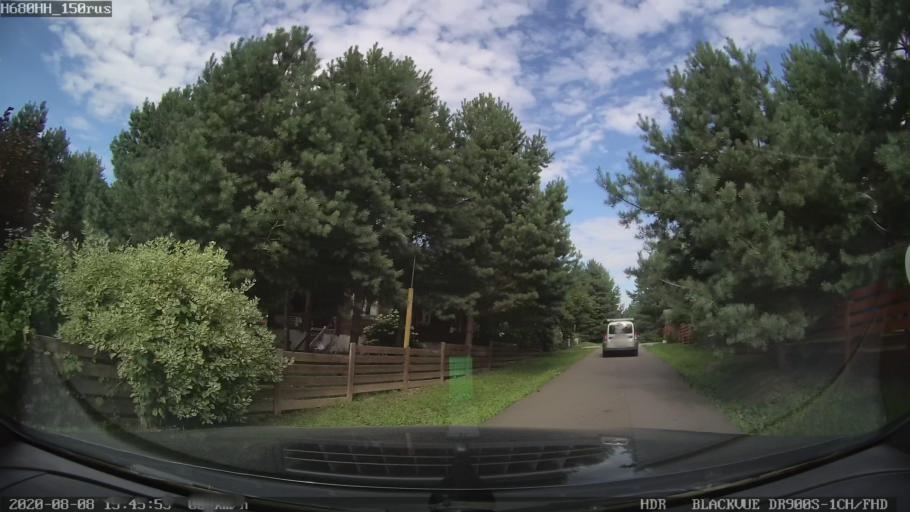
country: RU
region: Tula
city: Zaokskiy
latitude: 54.7349
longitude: 37.3333
